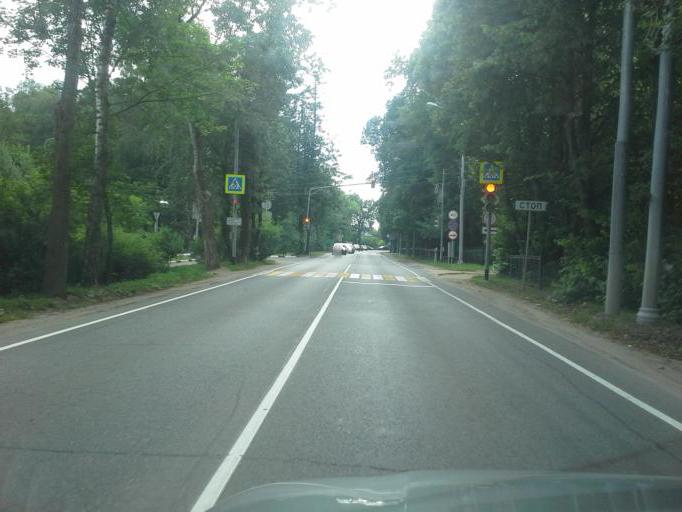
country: RU
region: Moskovskaya
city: Barvikha
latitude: 55.7238
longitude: 37.2768
